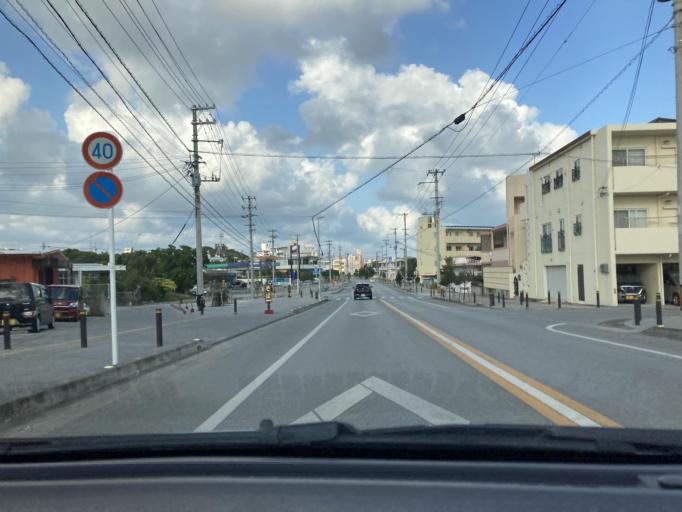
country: JP
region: Okinawa
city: Tomigusuku
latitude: 26.1500
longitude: 127.7148
